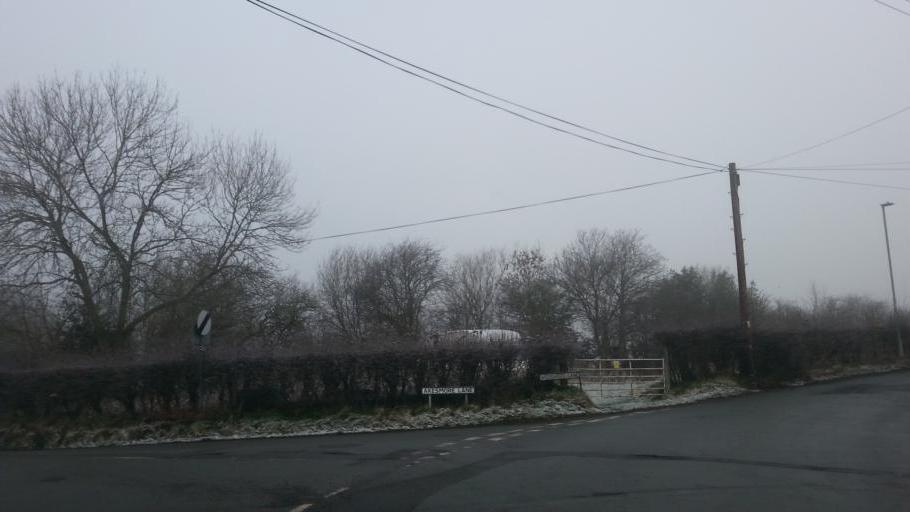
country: GB
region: England
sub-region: Staffordshire
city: Biddulph
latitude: 53.1229
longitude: -2.1798
